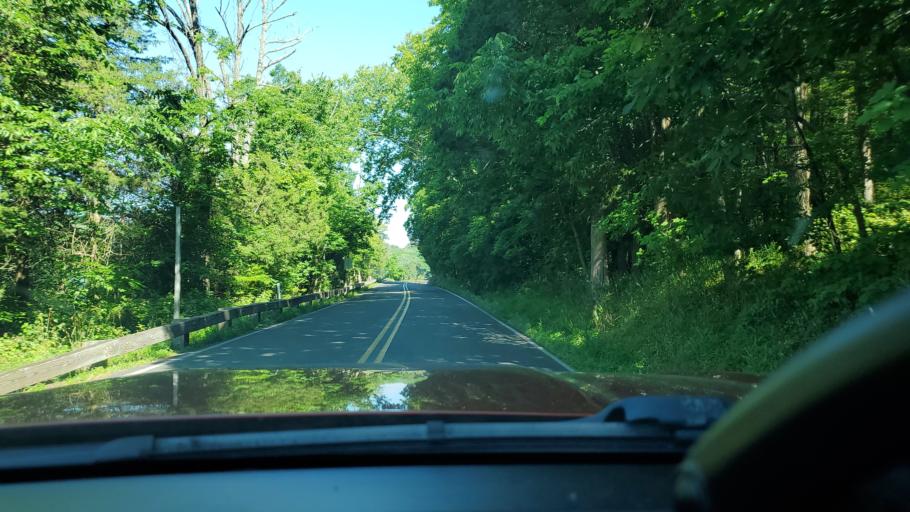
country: US
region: Pennsylvania
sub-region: Montgomery County
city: Red Hill
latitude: 40.3619
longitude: -75.5062
